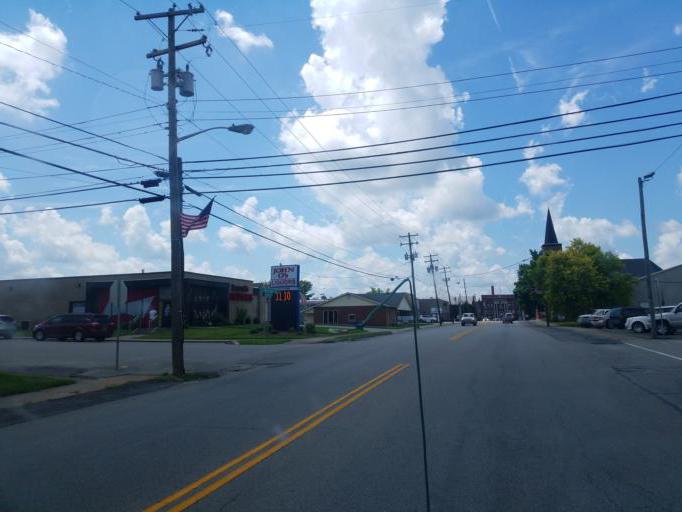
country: US
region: Kentucky
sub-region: Grayson County
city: Leitchfield
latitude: 37.4831
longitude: -86.2934
